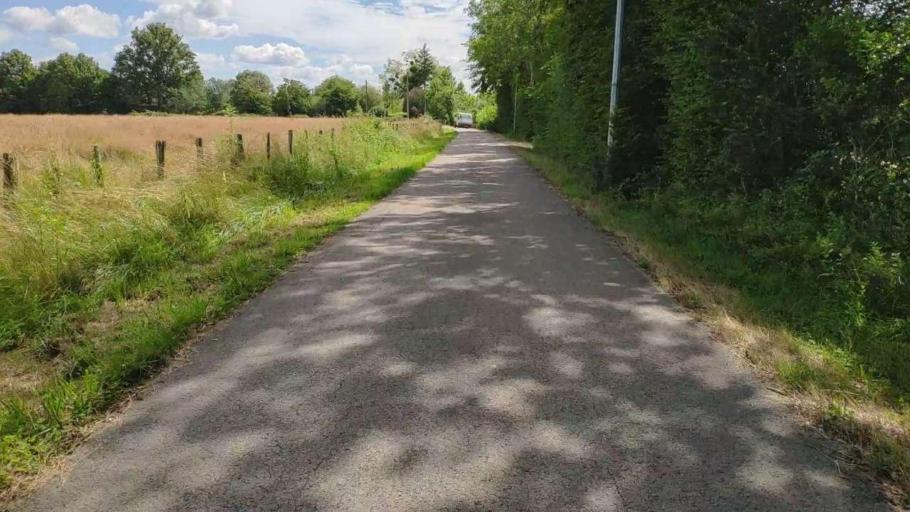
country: FR
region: Franche-Comte
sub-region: Departement du Jura
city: Bletterans
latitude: 46.8260
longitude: 5.4485
